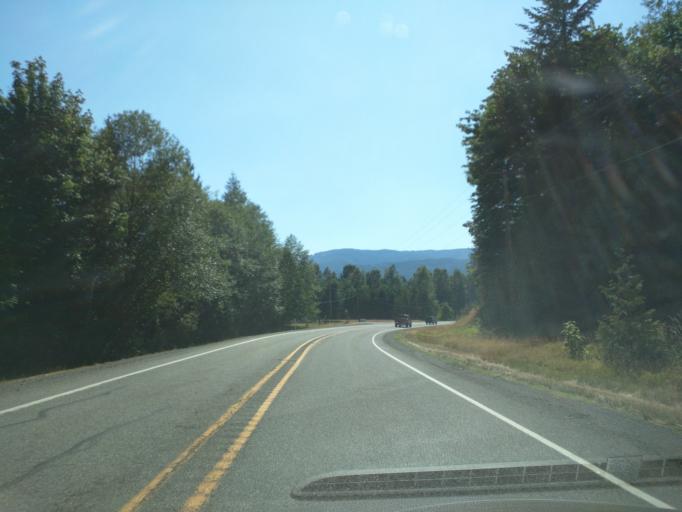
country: US
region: Washington
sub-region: Whatcom County
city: Peaceful Valley
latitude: 48.9164
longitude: -122.1182
